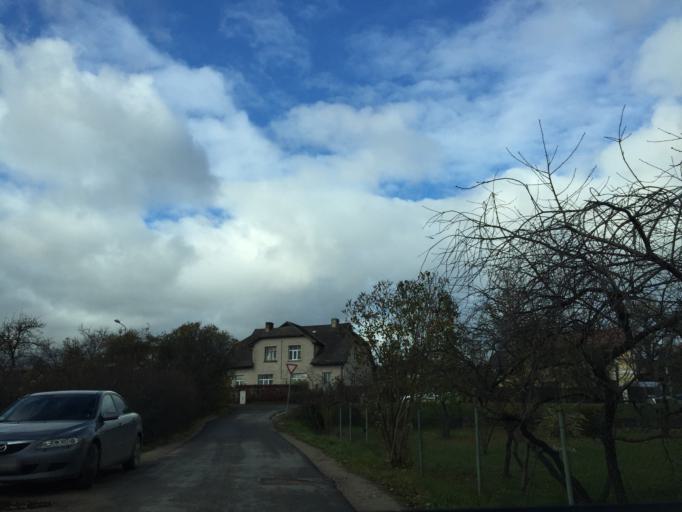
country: LV
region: Tukuma Rajons
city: Tukums
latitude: 56.9682
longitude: 23.1774
